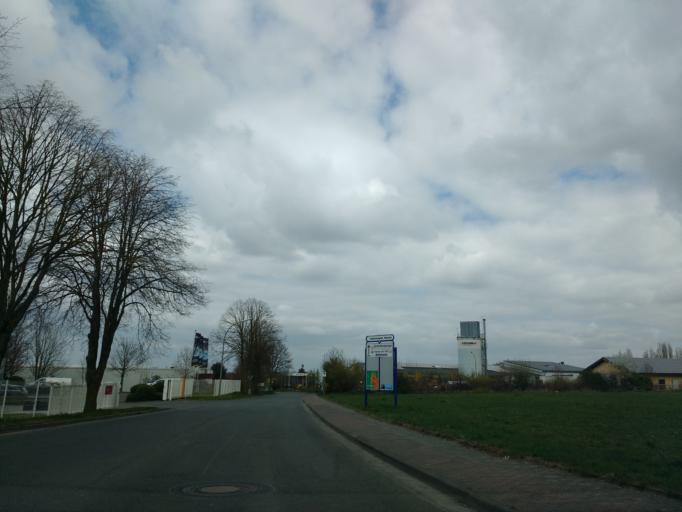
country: DE
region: North Rhine-Westphalia
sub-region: Regierungsbezirk Detmold
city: Wunnenberg
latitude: 51.5732
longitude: 8.7165
